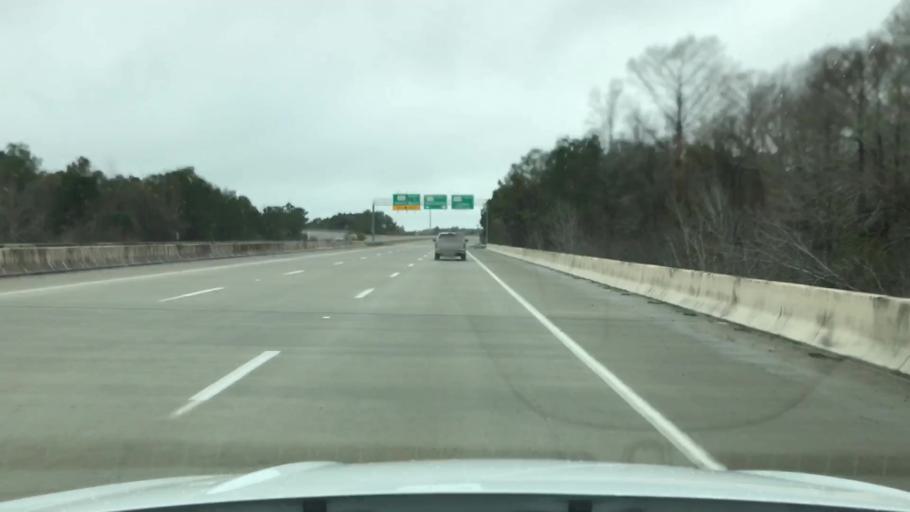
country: US
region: South Carolina
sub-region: Horry County
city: Forestbrook
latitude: 33.7416
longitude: -78.9442
